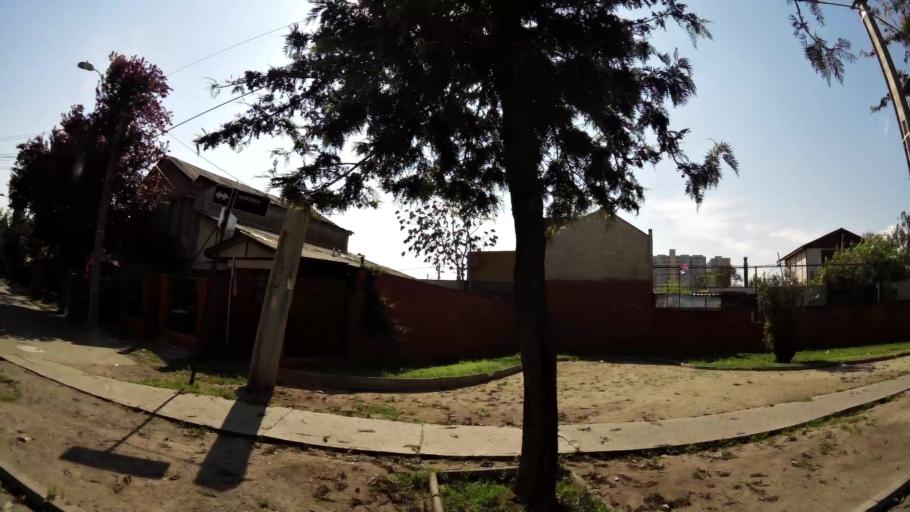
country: CL
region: Santiago Metropolitan
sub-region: Provincia de Santiago
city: La Pintana
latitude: -33.5513
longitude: -70.5928
